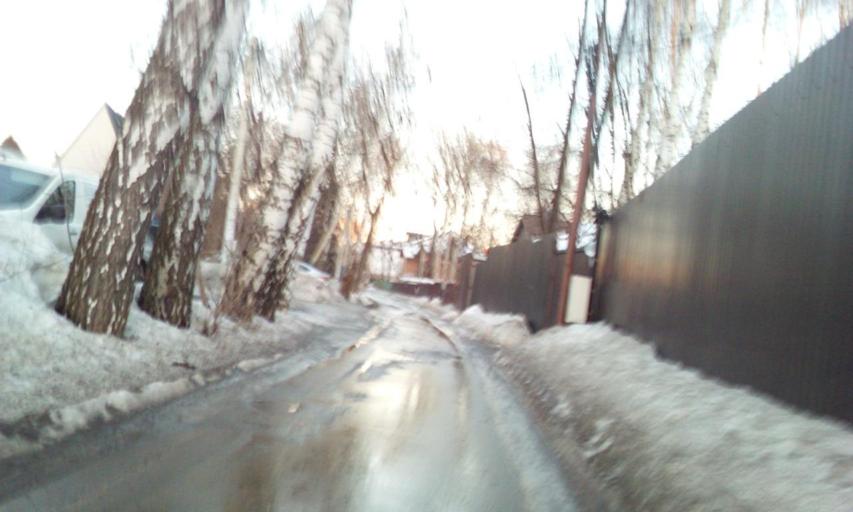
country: RU
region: Moscow
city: Novo-Peredelkino
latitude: 55.6474
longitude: 37.3225
